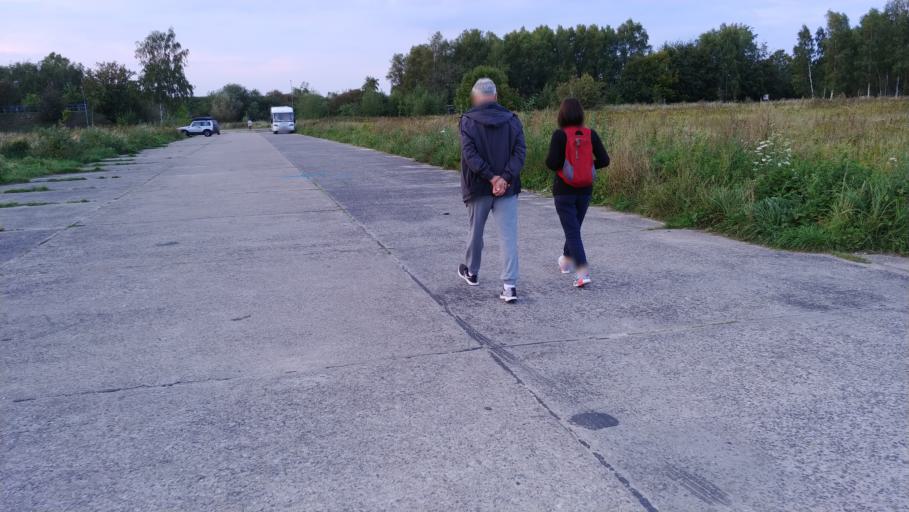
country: PL
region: West Pomeranian Voivodeship
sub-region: Powiat kolobrzeski
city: Kolobrzeg
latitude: 54.1970
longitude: 15.6637
